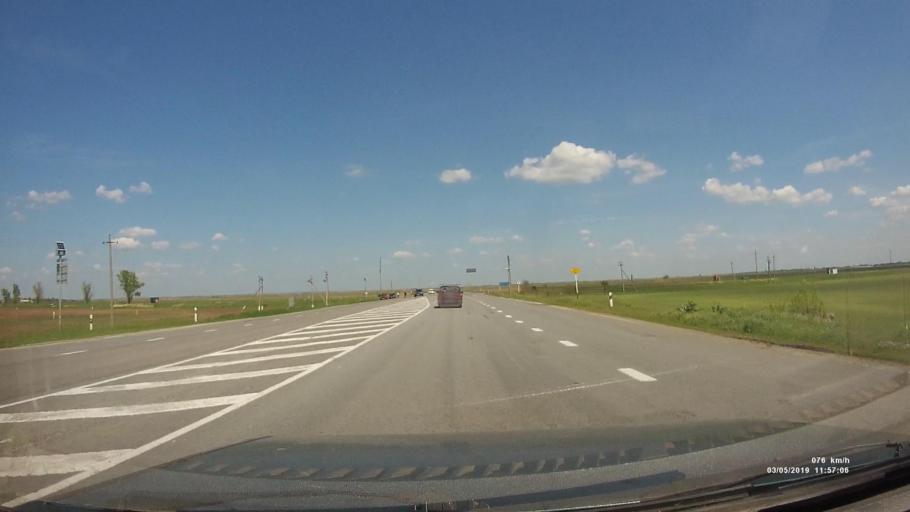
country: RU
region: Rostov
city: Bagayevskaya
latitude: 47.2027
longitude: 40.3069
